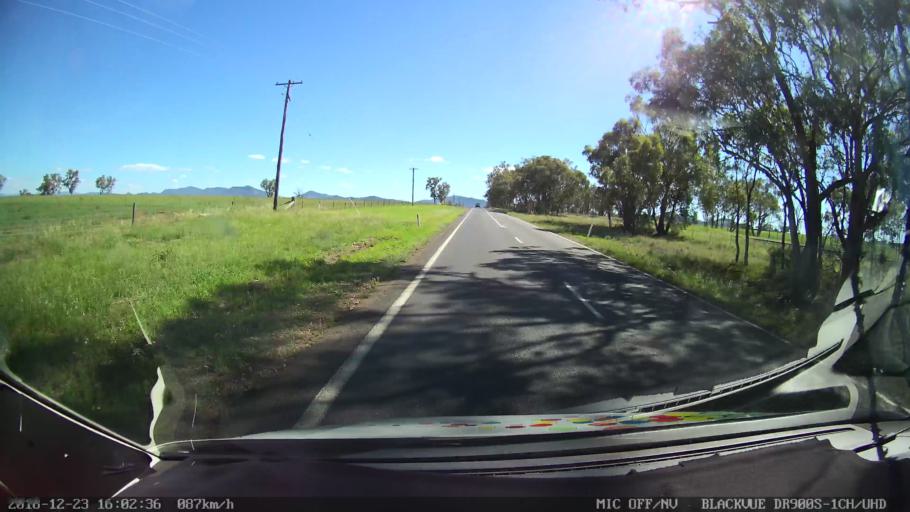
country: AU
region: New South Wales
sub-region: Tamworth Municipality
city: Phillip
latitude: -31.2340
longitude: 150.8077
